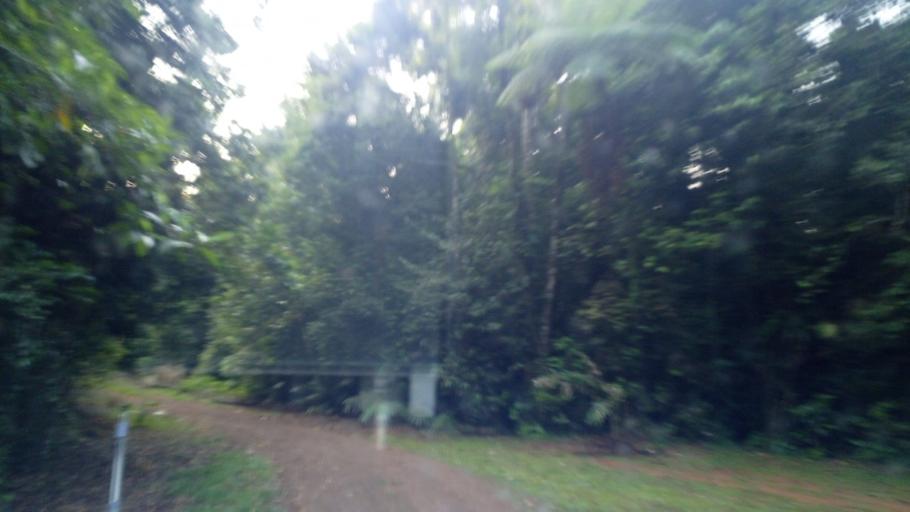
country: AU
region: Queensland
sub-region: Cassowary Coast
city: Innisfail
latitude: -17.3791
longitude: 145.7627
